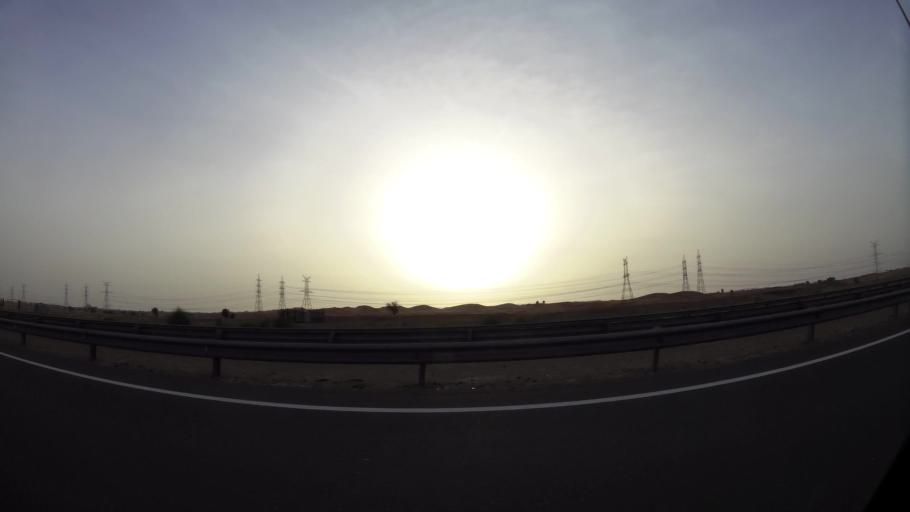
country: OM
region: Al Buraimi
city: Al Buraymi
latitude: 24.3104
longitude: 55.7471
